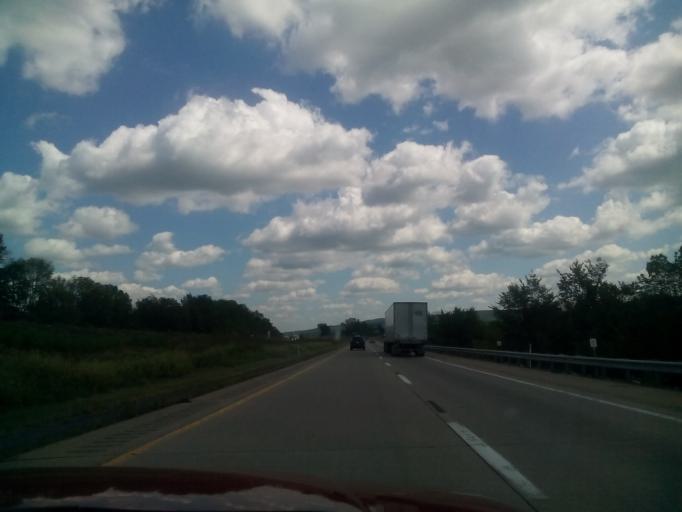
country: US
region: Pennsylvania
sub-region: Northumberland County
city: Riverside
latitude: 40.9898
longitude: -76.6697
